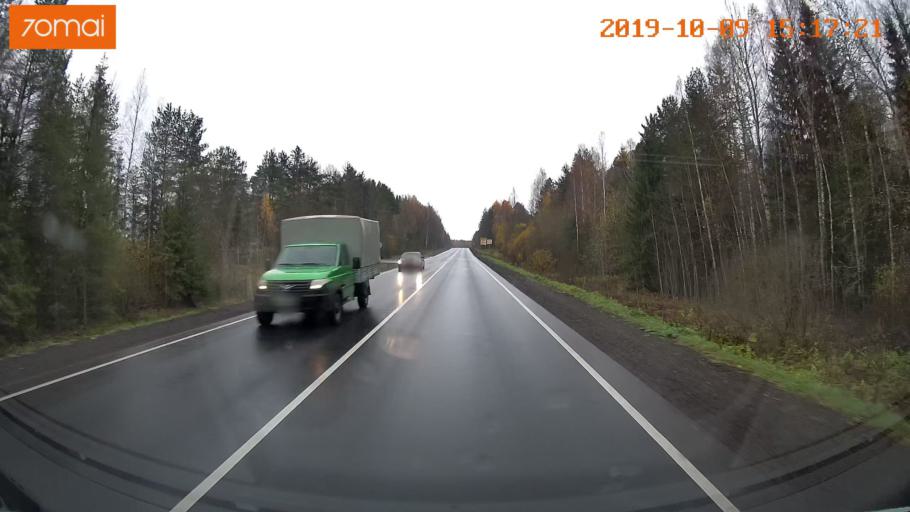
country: RU
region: Kostroma
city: Susanino
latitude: 58.0994
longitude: 41.5830
